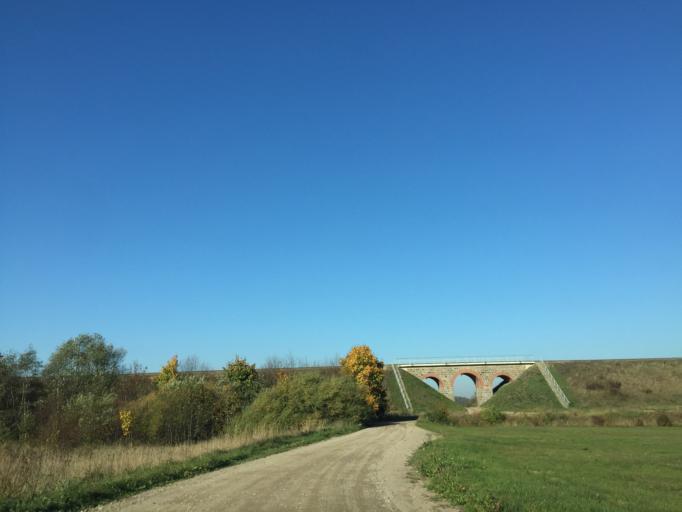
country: LT
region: Klaipedos apskritis
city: Kretinga
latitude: 55.8618
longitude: 21.2153
